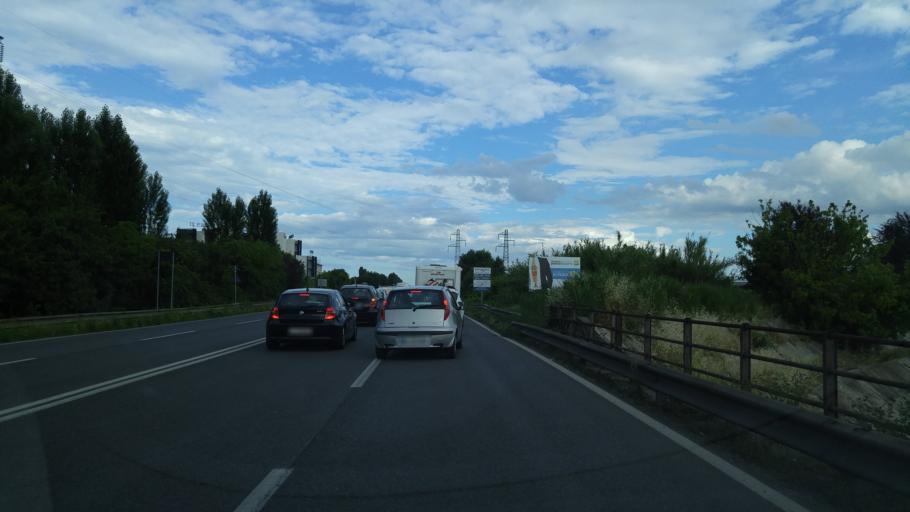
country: IT
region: Emilia-Romagna
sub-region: Provincia di Rimini
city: Rimini
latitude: 44.0454
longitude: 12.5547
